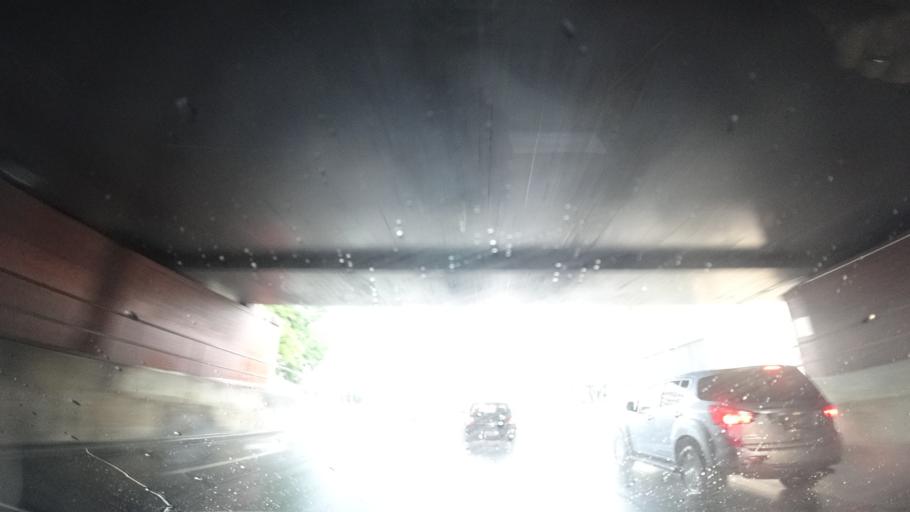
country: AU
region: Queensland
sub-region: Brisbane
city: Spring Hill
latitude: -27.4654
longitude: 153.0159
